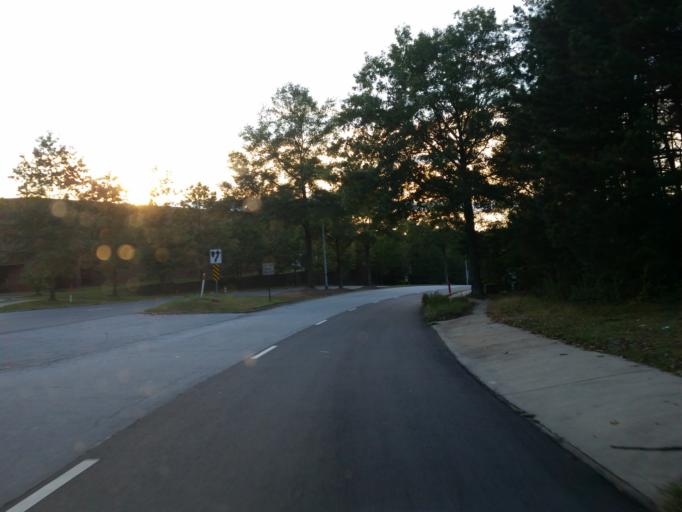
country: US
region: Georgia
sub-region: Cobb County
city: Vinings
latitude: 33.8274
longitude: -84.4986
